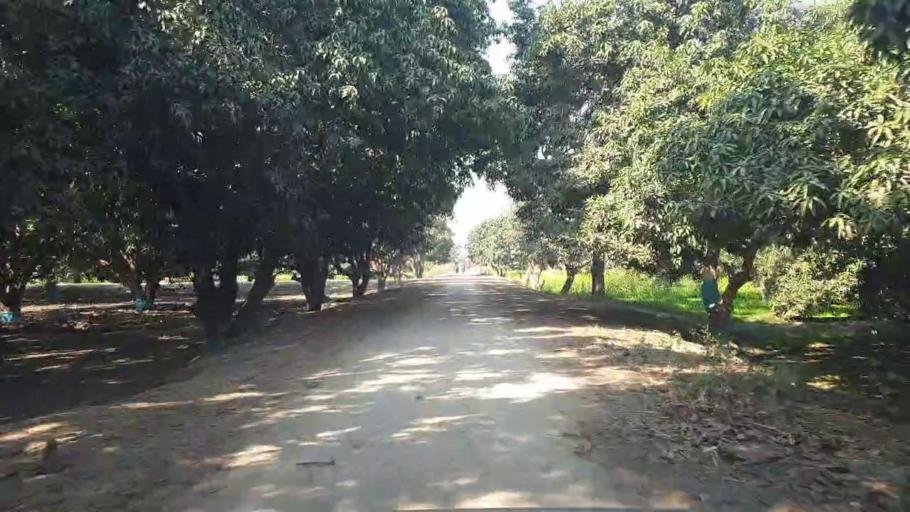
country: PK
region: Sindh
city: Tando Allahyar
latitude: 25.4708
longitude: 68.7793
